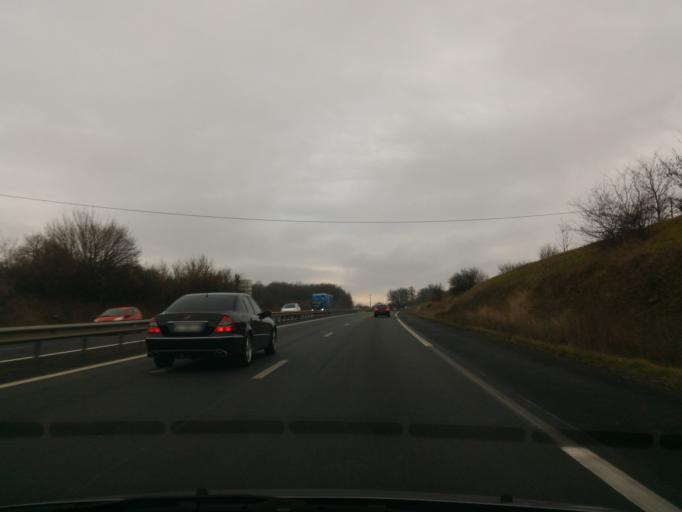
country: FR
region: Poitou-Charentes
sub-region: Departement de la Vienne
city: Fontaine-le-Comte
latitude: 46.5205
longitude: 0.2796
